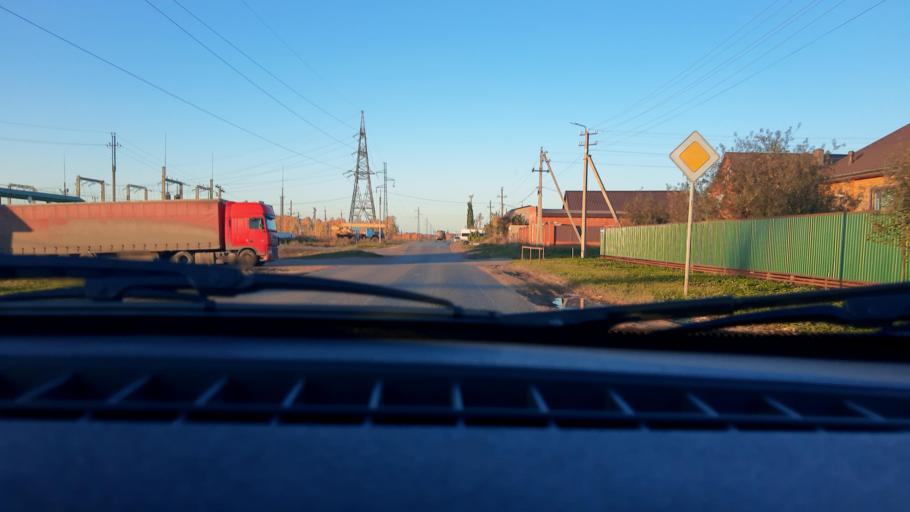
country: RU
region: Bashkortostan
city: Ufa
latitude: 54.8419
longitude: 55.9991
